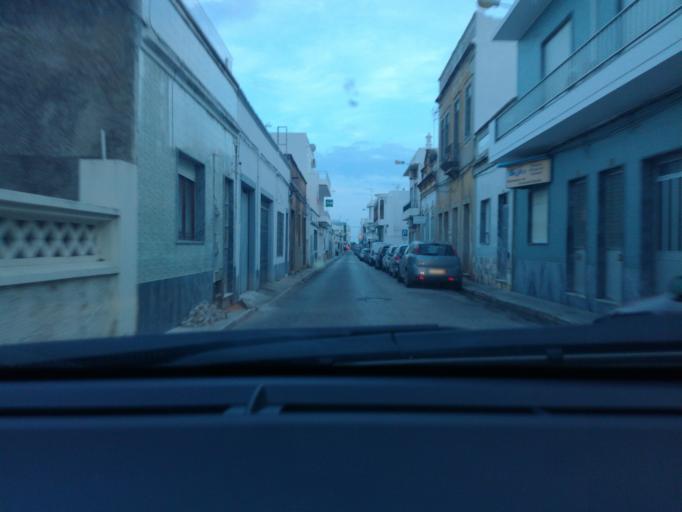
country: PT
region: Faro
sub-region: Olhao
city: Laranjeiro
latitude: 37.0572
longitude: -7.7483
